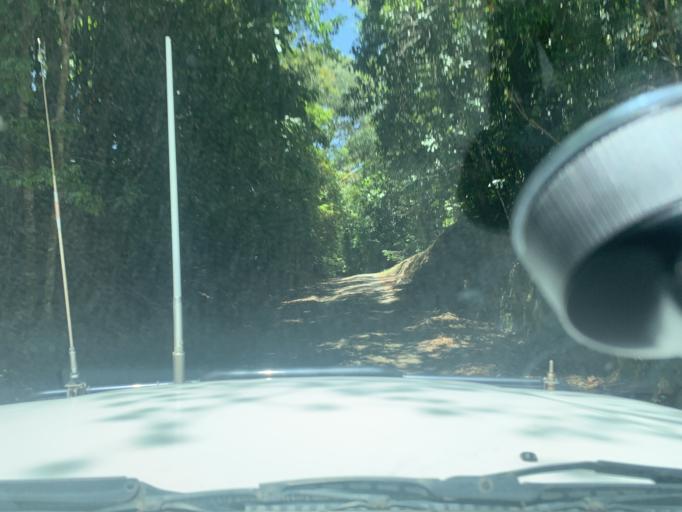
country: AU
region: Queensland
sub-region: Cairns
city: Redlynch
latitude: -16.9607
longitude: 145.6460
